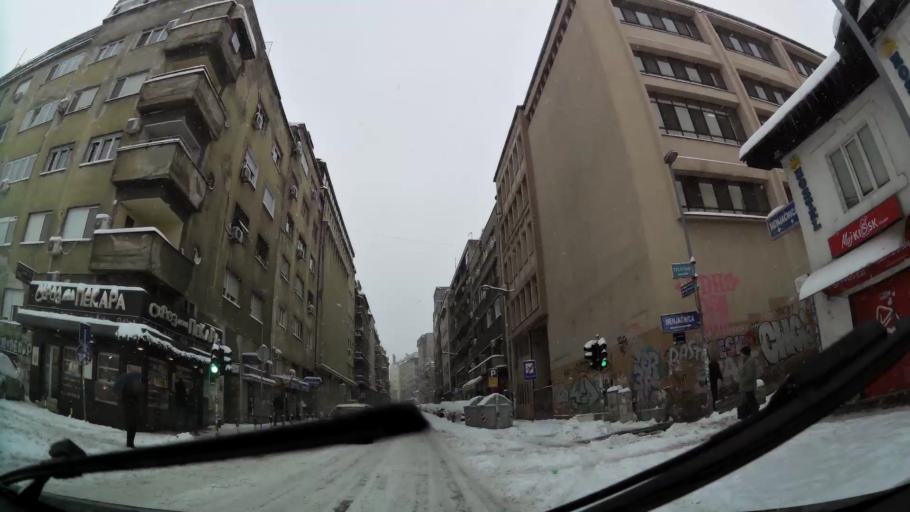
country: RS
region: Central Serbia
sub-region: Belgrade
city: Stari Grad
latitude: 44.8121
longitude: 20.4559
